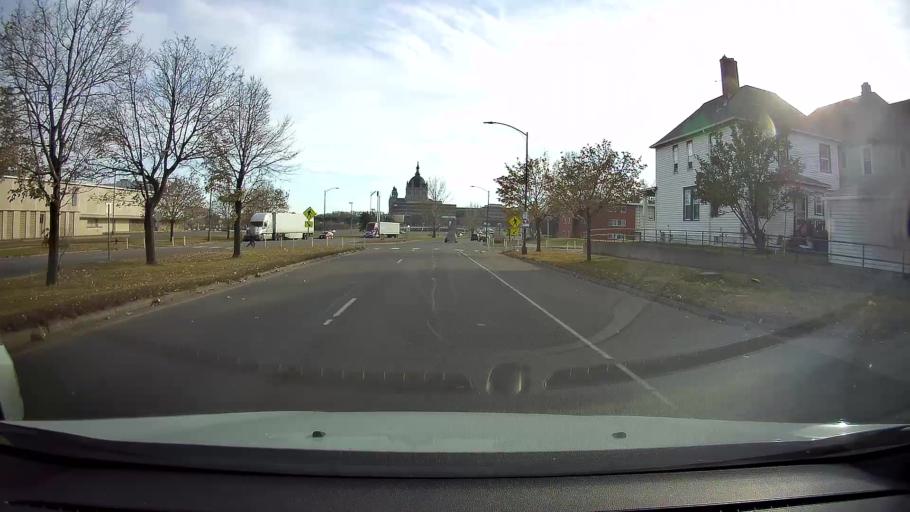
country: US
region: Minnesota
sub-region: Ramsey County
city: Saint Paul
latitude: 44.9545
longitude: -93.1095
